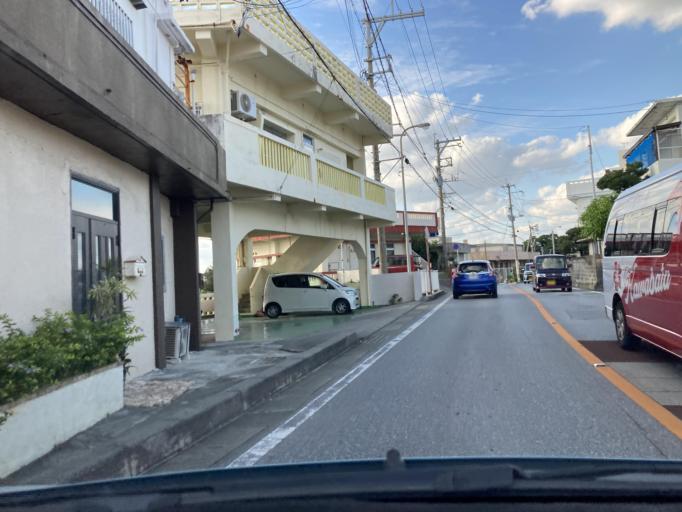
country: JP
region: Okinawa
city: Chatan
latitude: 26.3145
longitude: 127.7691
